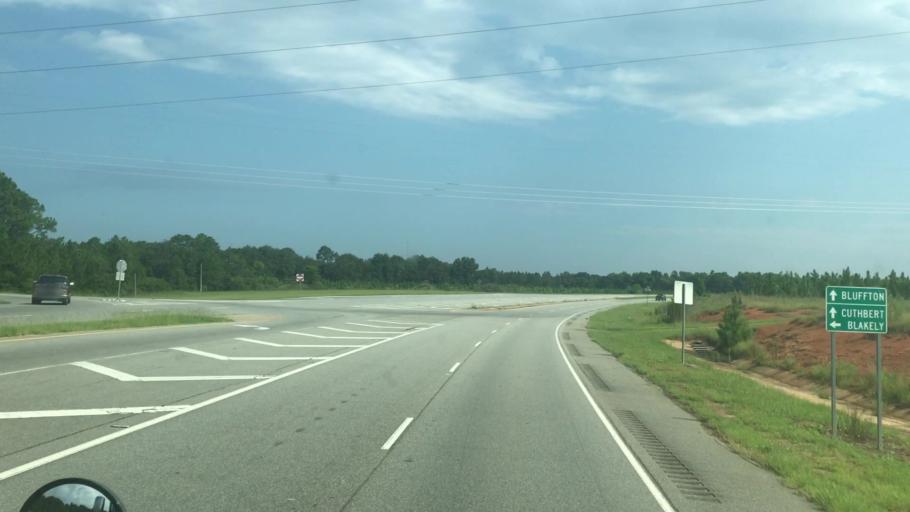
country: US
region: Georgia
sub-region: Early County
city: Blakely
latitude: 31.3574
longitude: -84.9230
